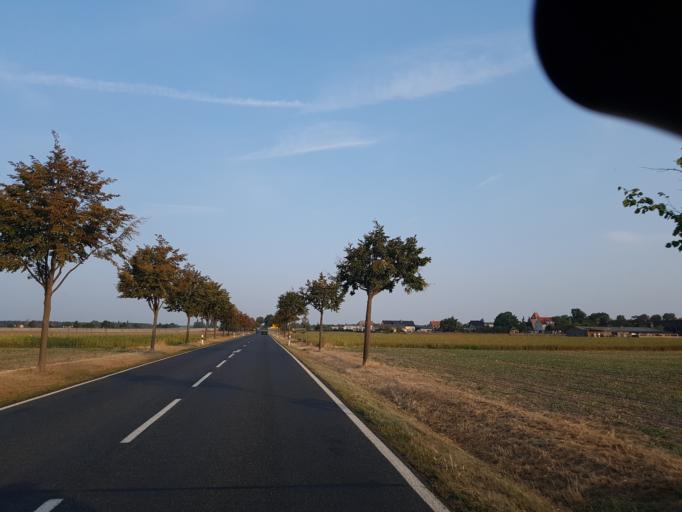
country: DE
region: Saxony
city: Elsnig
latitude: 51.6067
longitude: 12.9310
